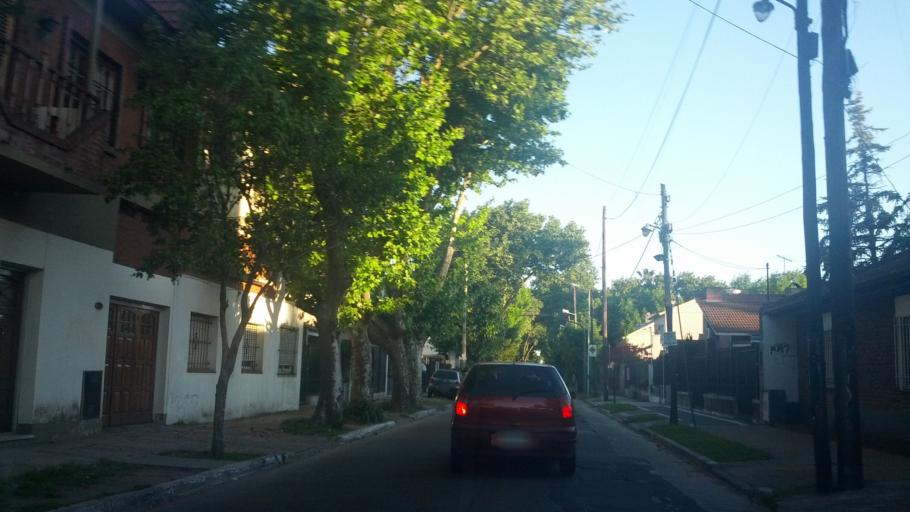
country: AR
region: Buenos Aires
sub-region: Partido de Lomas de Zamora
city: Lomas de Zamora
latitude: -34.7780
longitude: -58.3929
